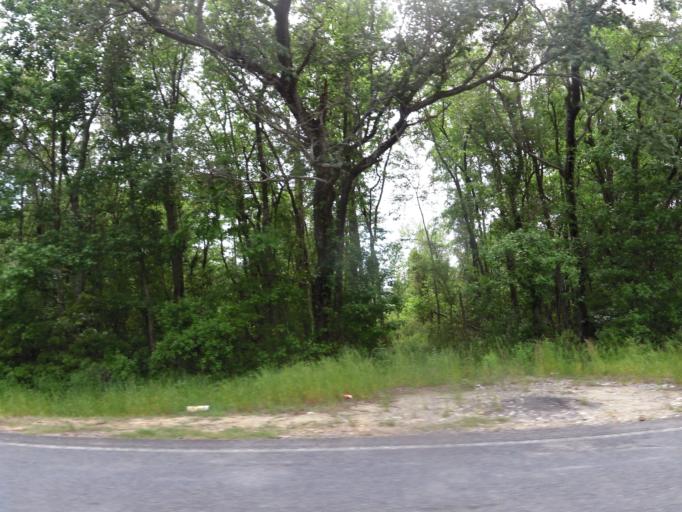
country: US
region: Georgia
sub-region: Candler County
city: Metter
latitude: 32.3809
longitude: -82.1683
